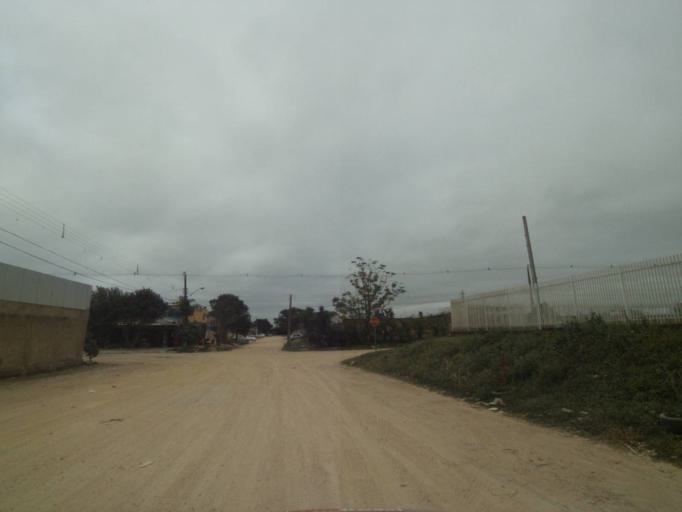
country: BR
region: Parana
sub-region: Sao Jose Dos Pinhais
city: Sao Jose dos Pinhais
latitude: -25.5053
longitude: -49.2150
